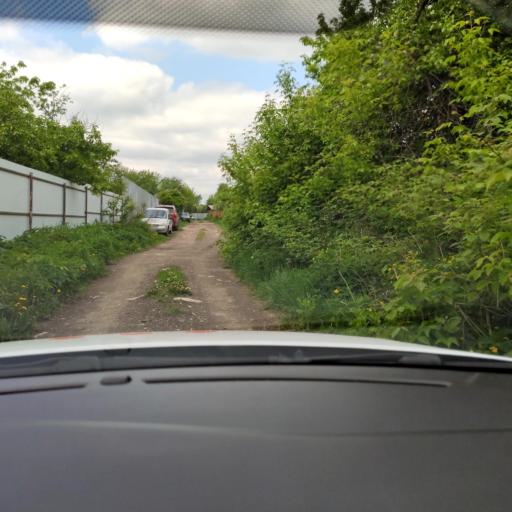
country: RU
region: Tatarstan
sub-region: Gorod Kazan'
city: Kazan
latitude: 55.8695
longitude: 49.1056
